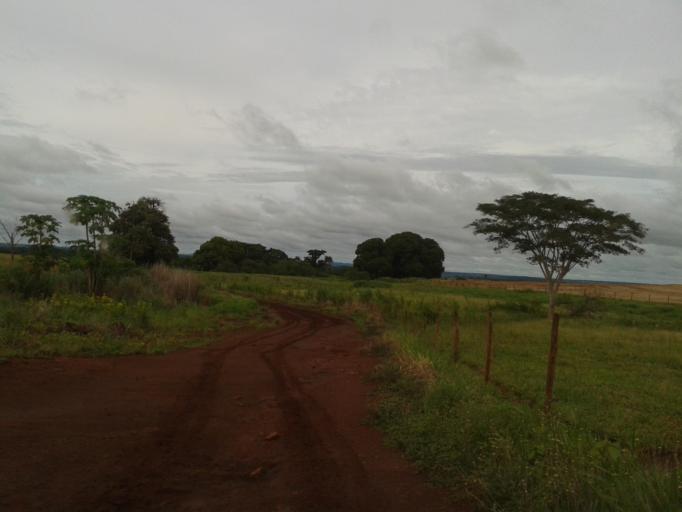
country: BR
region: Minas Gerais
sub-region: Capinopolis
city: Capinopolis
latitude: -18.7695
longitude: -49.7669
